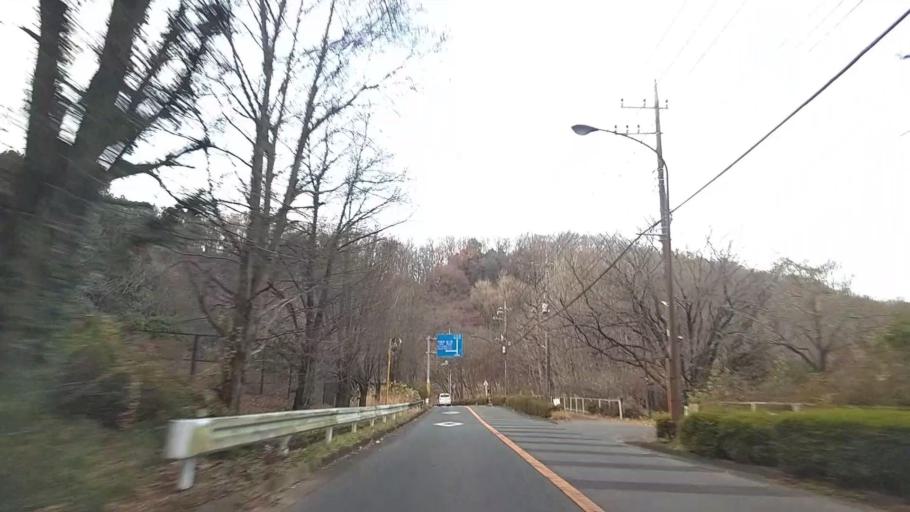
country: JP
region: Kanagawa
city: Atsugi
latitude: 35.4449
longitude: 139.3215
